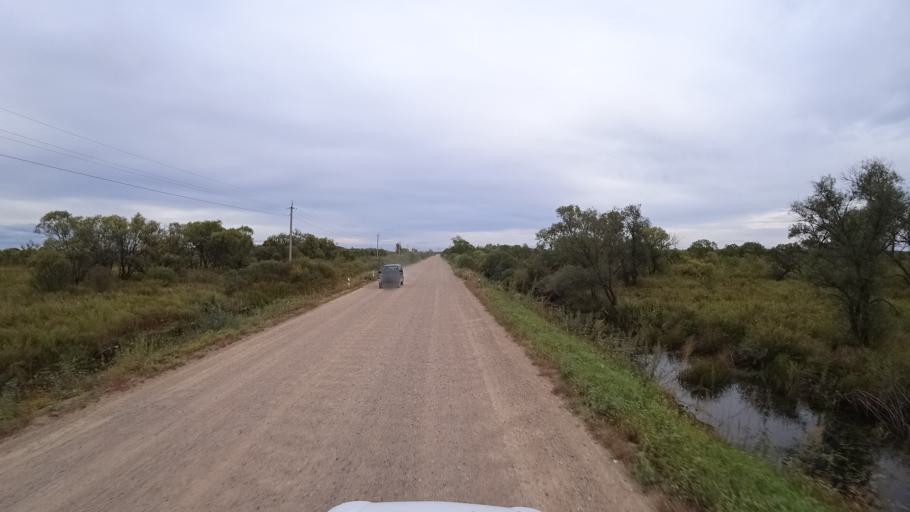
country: RU
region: Amur
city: Arkhara
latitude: 49.4314
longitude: 130.2264
